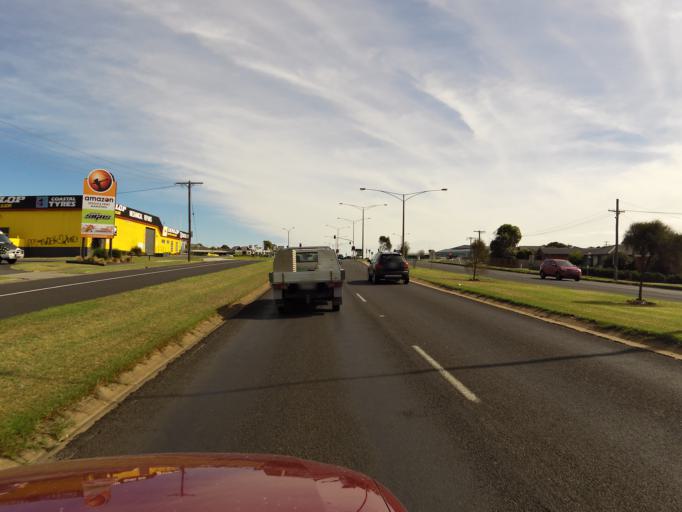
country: AU
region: Victoria
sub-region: Warrnambool
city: Warrnambool
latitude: -38.3653
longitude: 142.4610
